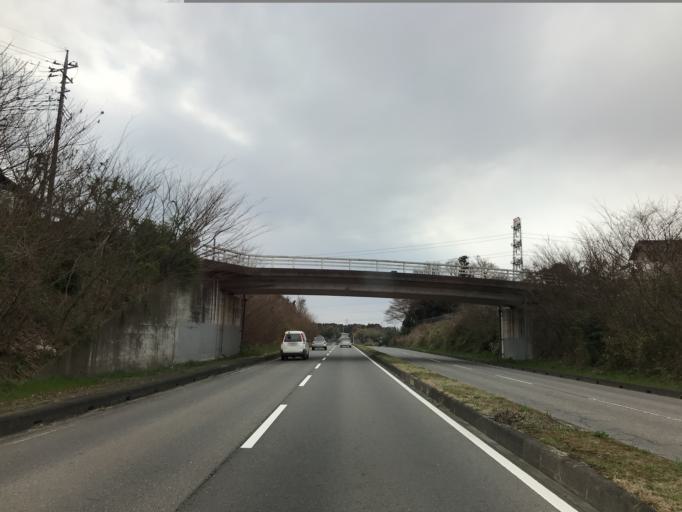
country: JP
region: Ibaraki
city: Ushiku
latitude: 36.0039
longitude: 140.0808
